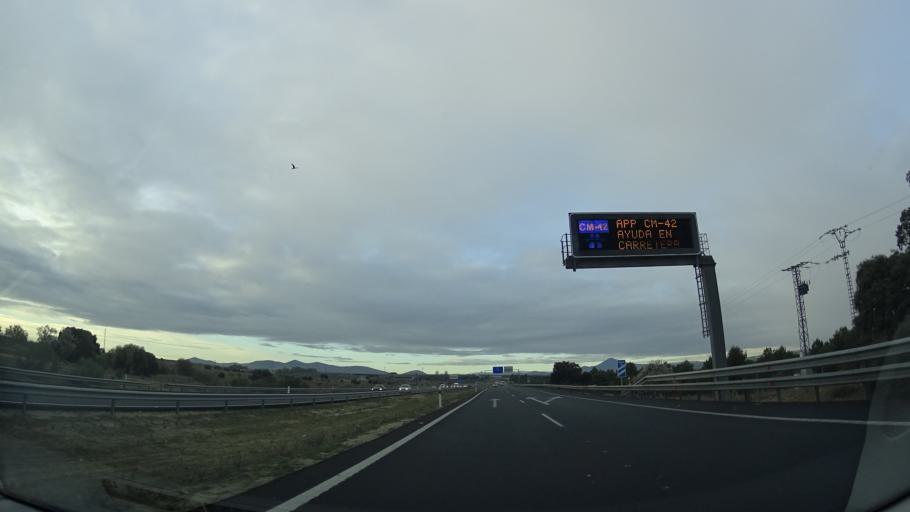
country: ES
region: Castille-La Mancha
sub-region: Province of Toledo
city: Burguillos de Toledo
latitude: 39.8282
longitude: -3.9810
